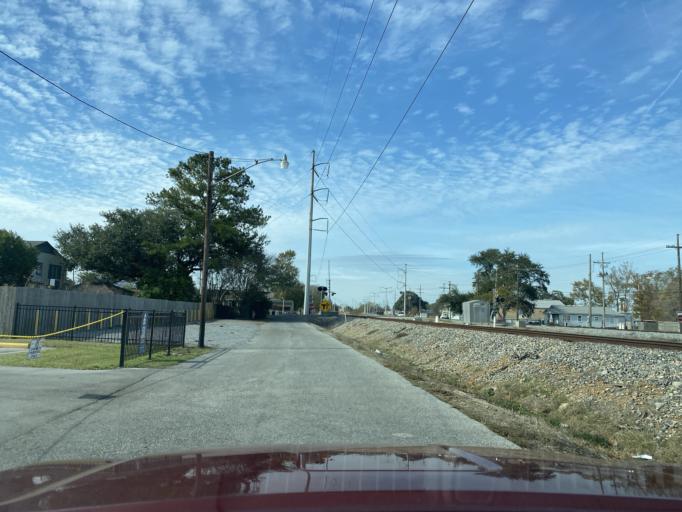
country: US
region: Louisiana
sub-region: Jefferson Parish
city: Kenner
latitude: 29.9759
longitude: -90.2476
